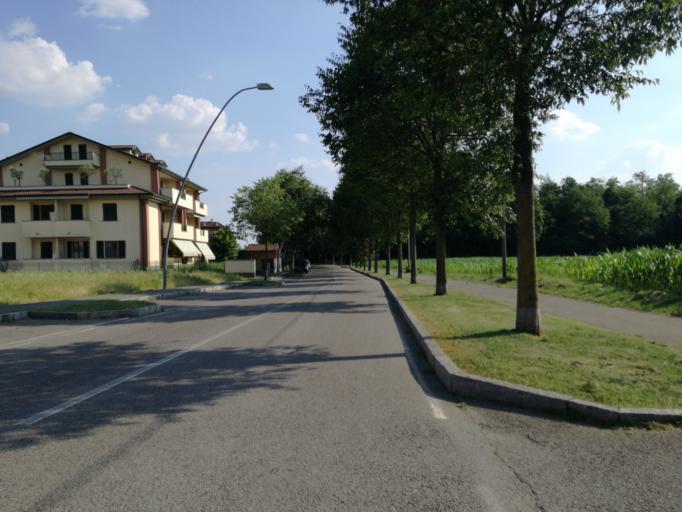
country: IT
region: Lombardy
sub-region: Provincia di Bergamo
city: Calusco d'Adda
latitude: 45.6916
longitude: 9.4582
